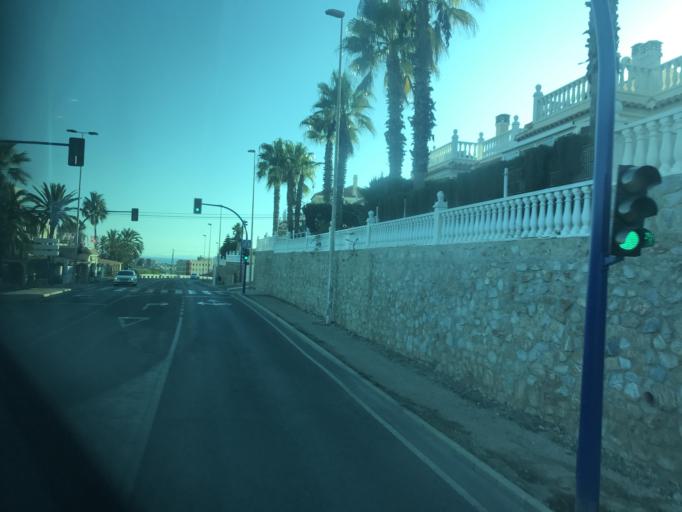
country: ES
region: Valencia
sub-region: Provincia de Alicante
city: Torrevieja
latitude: 37.9997
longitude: -0.6524
